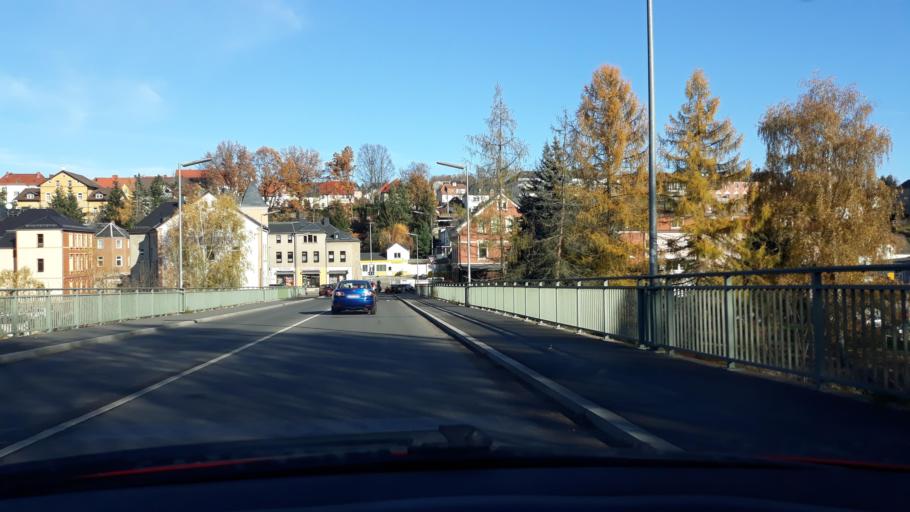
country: DE
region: Saxony
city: Wilkau-Hasslau
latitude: 50.6761
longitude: 12.5120
